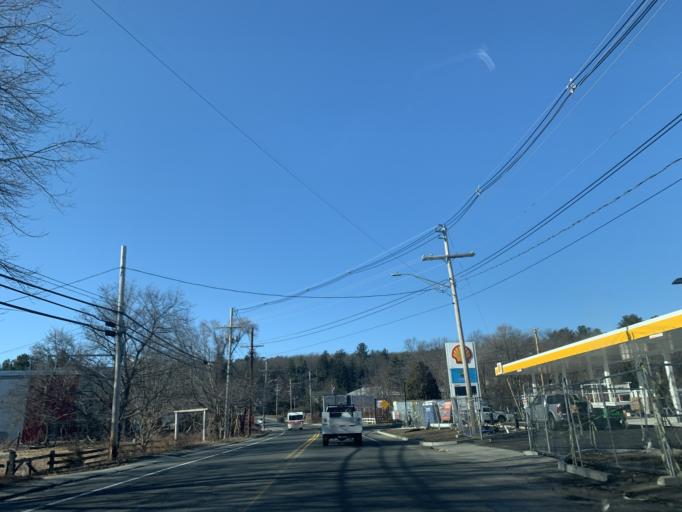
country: US
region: Massachusetts
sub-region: Middlesex County
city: Marlborough
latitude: 42.3487
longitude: -71.5164
